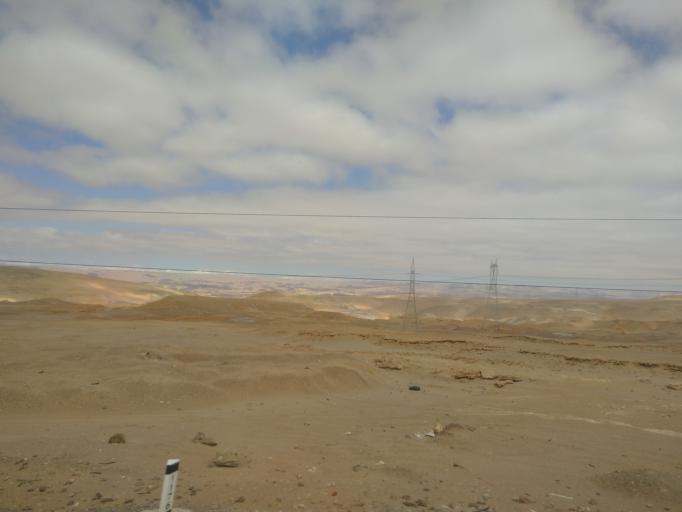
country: PE
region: Moquegua
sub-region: Provincia de Mariscal Nieto
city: Moquegua
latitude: -17.4405
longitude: -71.0509
